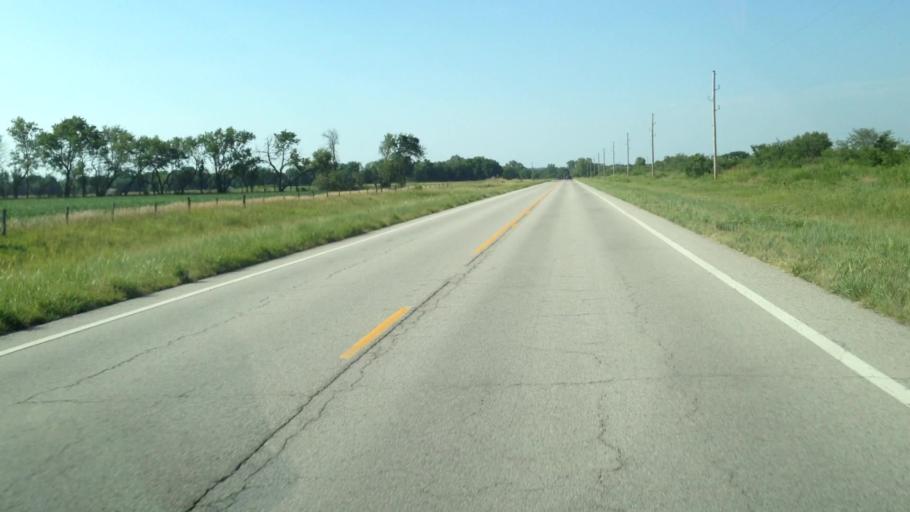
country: US
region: Kansas
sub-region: Allen County
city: Iola
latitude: 38.0144
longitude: -95.1709
